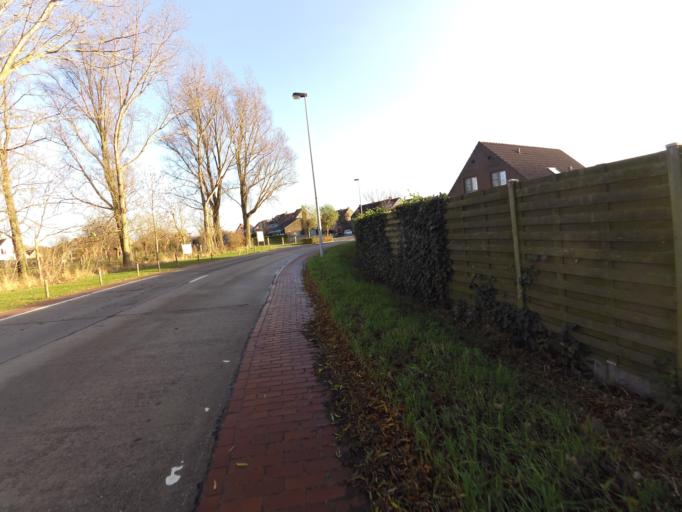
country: BE
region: Flanders
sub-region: Provincie West-Vlaanderen
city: Bredene
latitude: 51.2029
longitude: 2.9680
